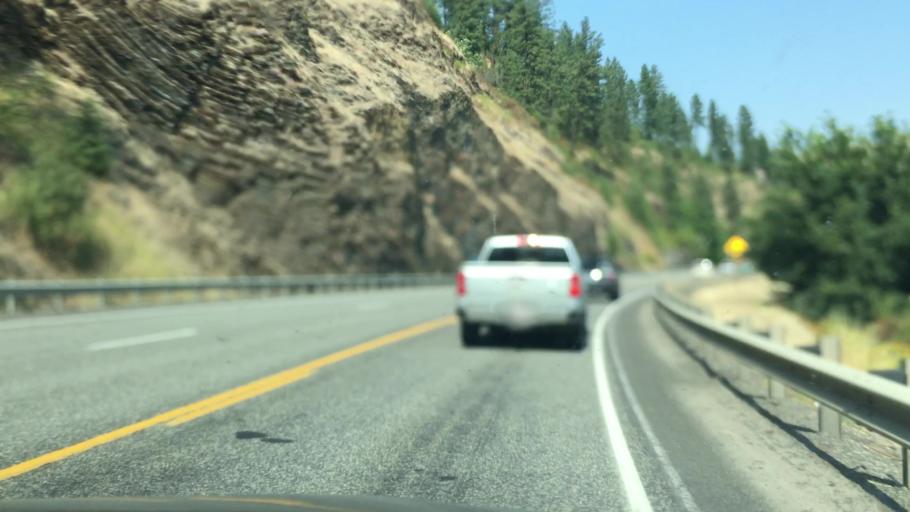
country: US
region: Idaho
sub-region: Nez Perce County
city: Lapwai
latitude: 46.5073
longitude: -116.5774
